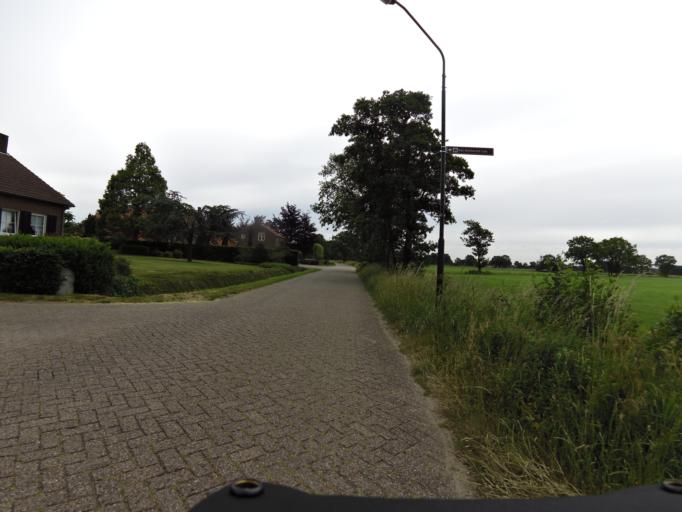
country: NL
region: North Brabant
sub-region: Gemeente Hilvarenbeek
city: Hilvarenbeek
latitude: 51.4865
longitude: 5.1092
